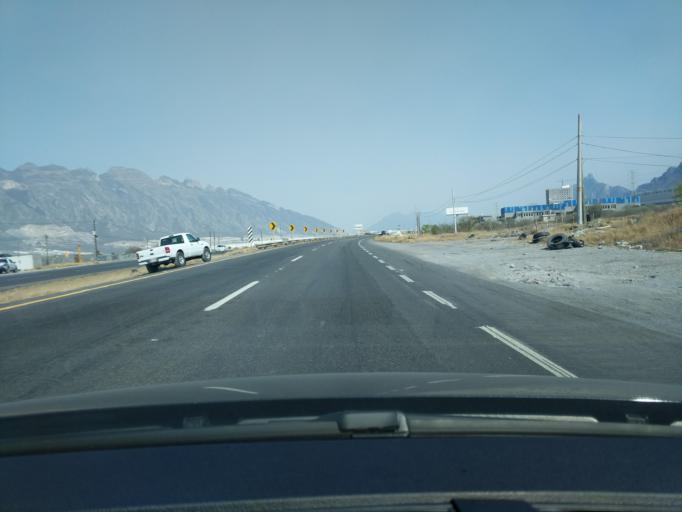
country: MX
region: Nuevo Leon
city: Santa Catarina
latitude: 25.6959
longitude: -100.5246
